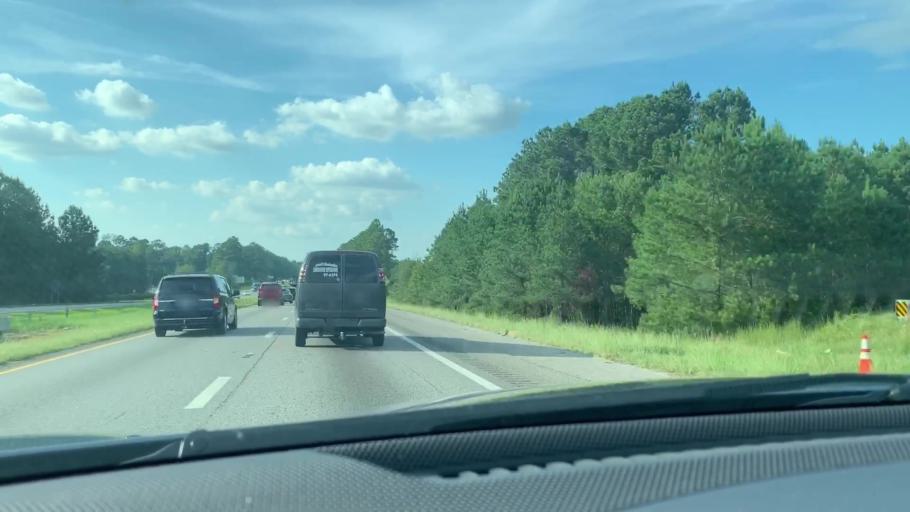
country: US
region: South Carolina
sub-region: Orangeburg County
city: Brookdale
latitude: 33.5205
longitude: -80.7915
